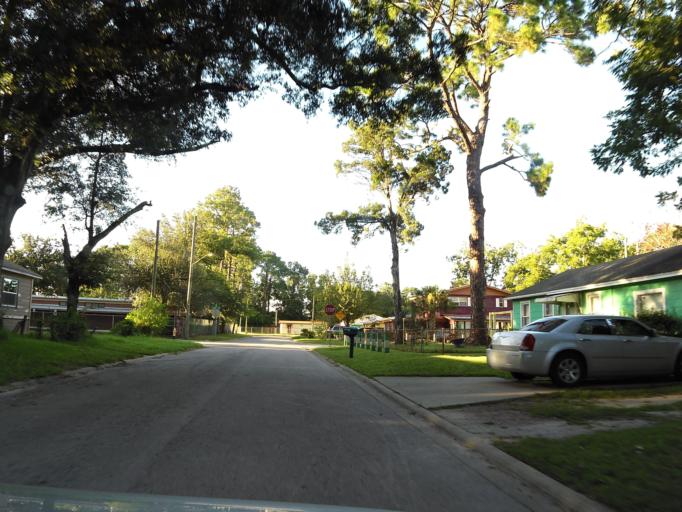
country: US
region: Florida
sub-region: Duval County
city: Jacksonville
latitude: 30.3542
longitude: -81.6999
